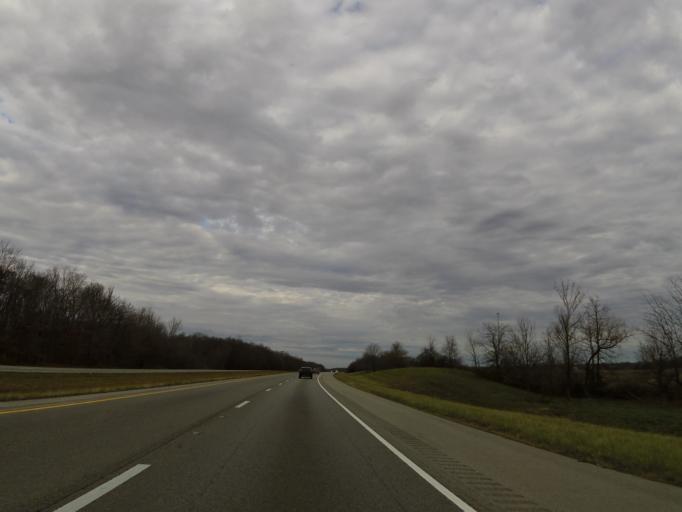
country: US
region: Illinois
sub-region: Clinton County
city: Wamac
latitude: 38.3648
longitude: -89.0853
